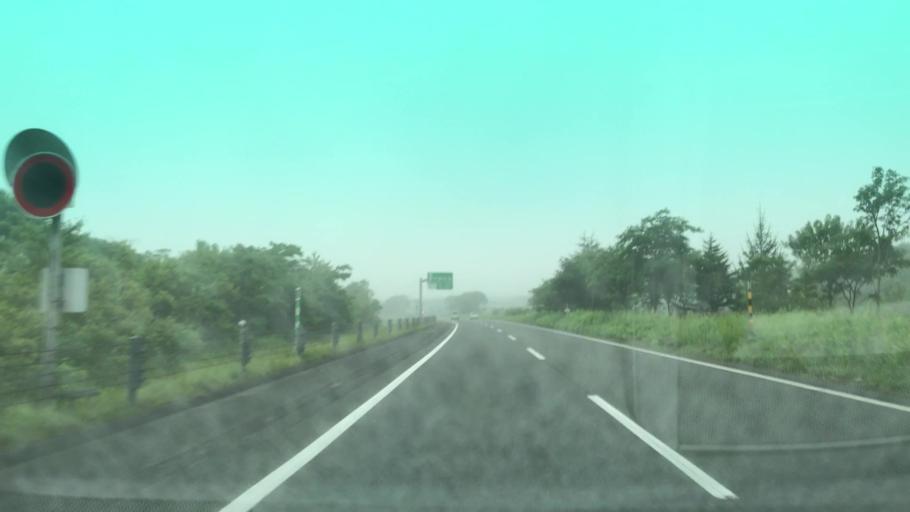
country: JP
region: Hokkaido
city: Chitose
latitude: 42.7809
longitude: 141.6269
